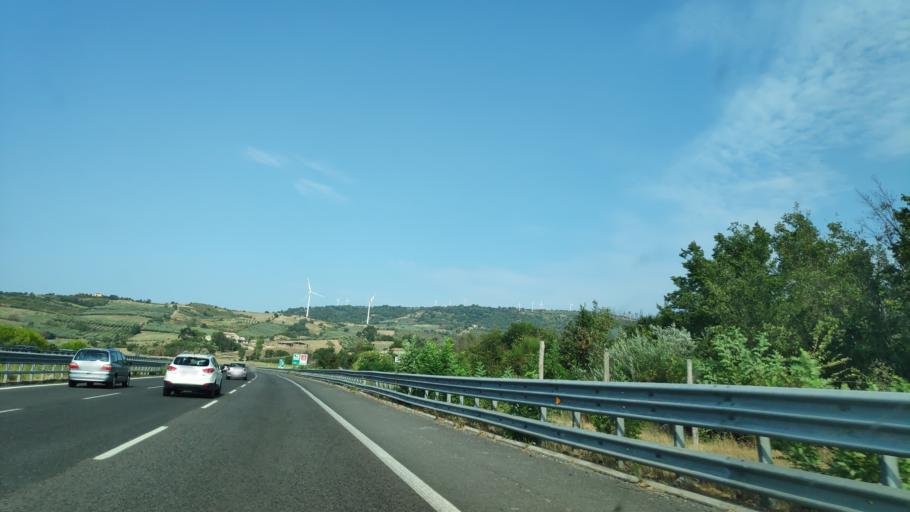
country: IT
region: Campania
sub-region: Provincia di Salerno
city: Serre
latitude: 40.6270
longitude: 15.1928
